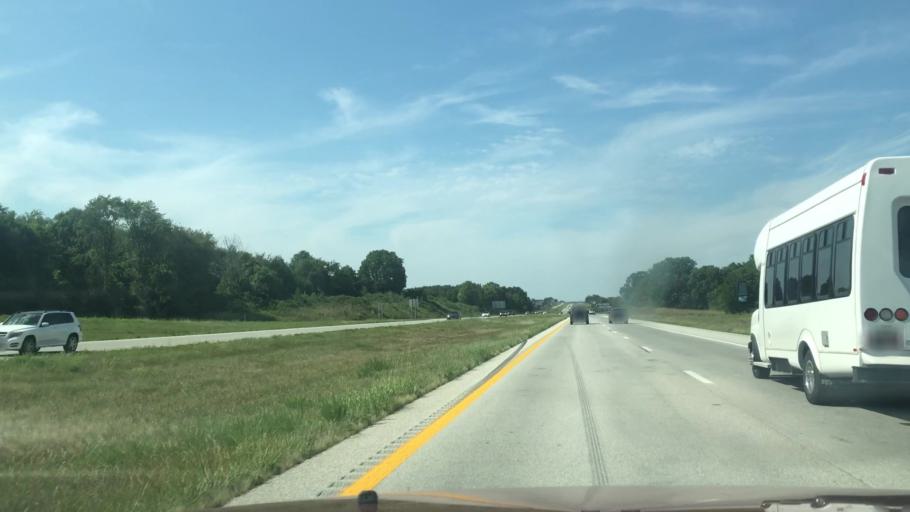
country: US
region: Missouri
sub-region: Christian County
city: Ozark
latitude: 36.9442
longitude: -93.2319
